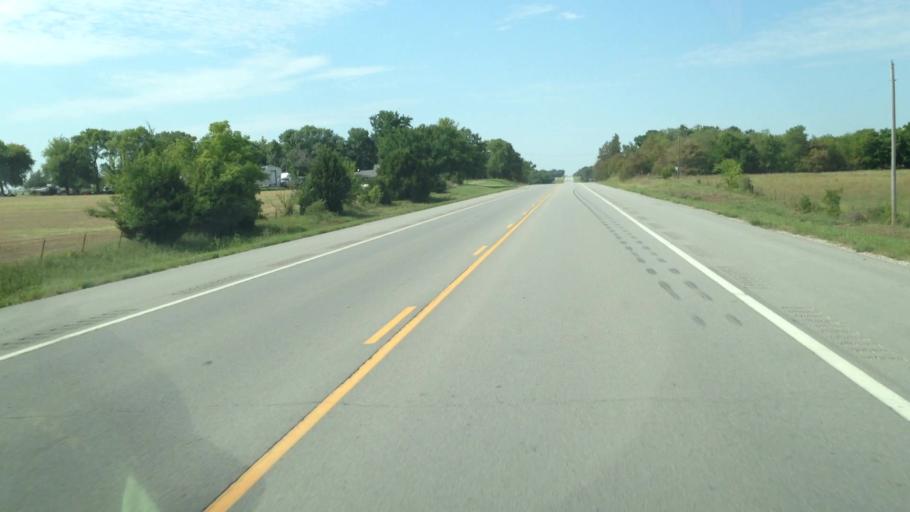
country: US
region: Kansas
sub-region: Labette County
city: Parsons
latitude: 37.2870
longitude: -95.2675
